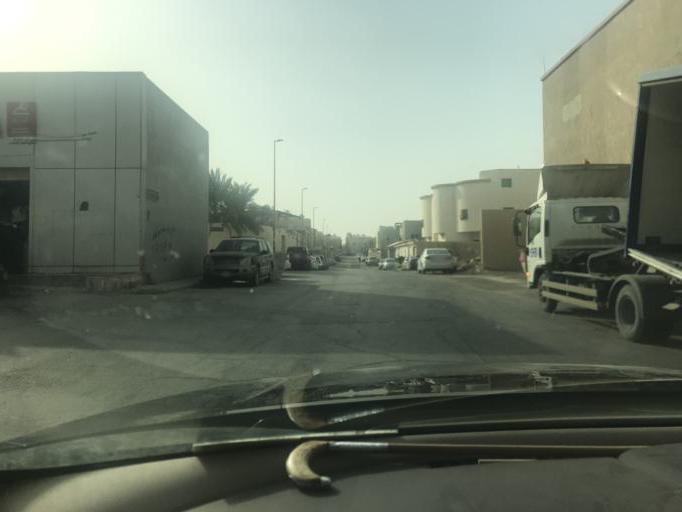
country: SA
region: Ar Riyad
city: Riyadh
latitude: 24.7199
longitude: 46.7693
